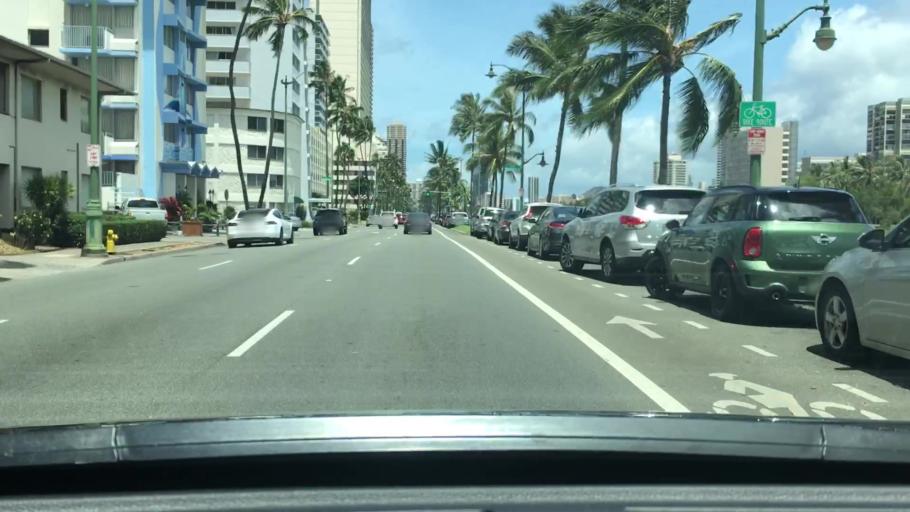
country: US
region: Hawaii
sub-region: Honolulu County
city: Honolulu
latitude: 21.2806
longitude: -157.8246
